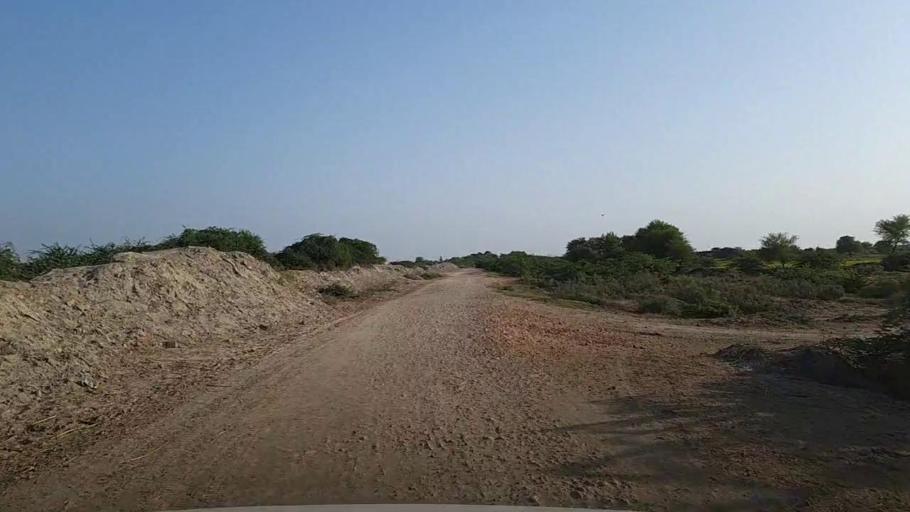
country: PK
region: Sindh
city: Kario
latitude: 24.7373
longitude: 68.6694
